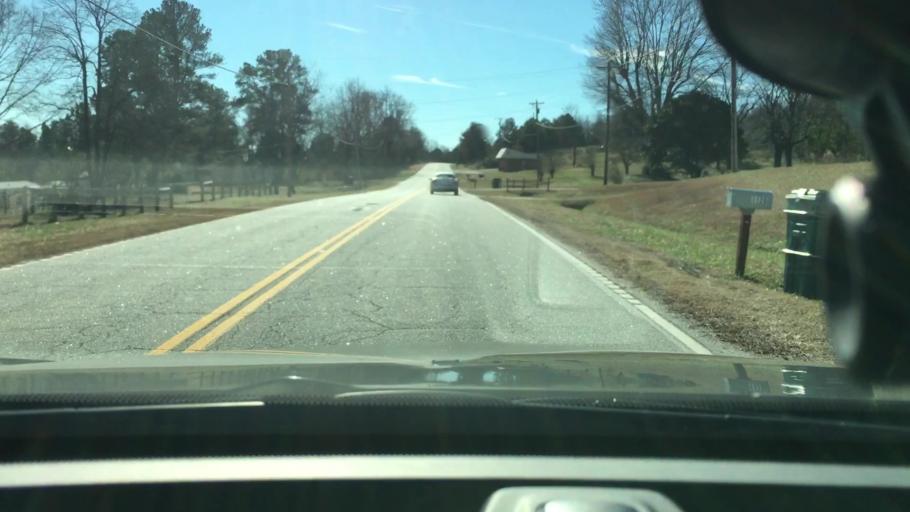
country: US
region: South Carolina
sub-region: Cherokee County
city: Gaffney
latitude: 35.0379
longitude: -81.6780
